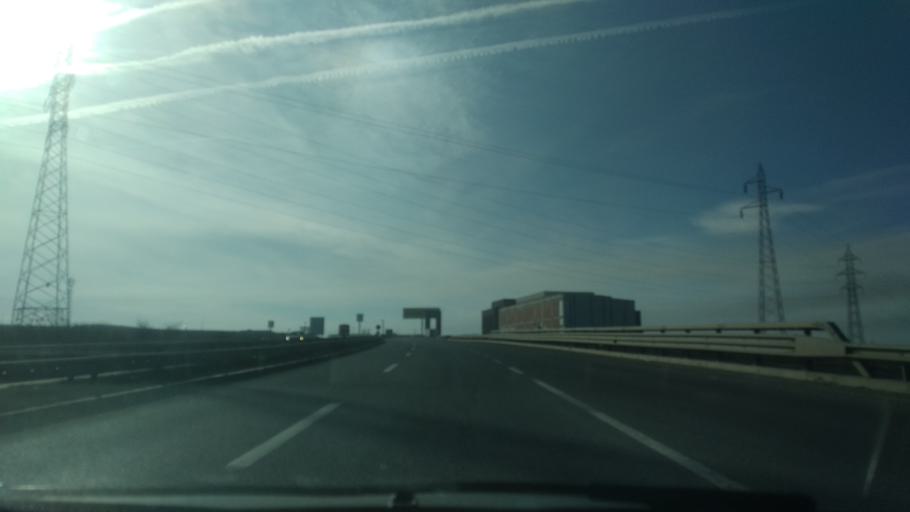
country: XK
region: Pristina
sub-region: Kosovo Polje
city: Kosovo Polje
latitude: 42.6810
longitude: 21.1163
